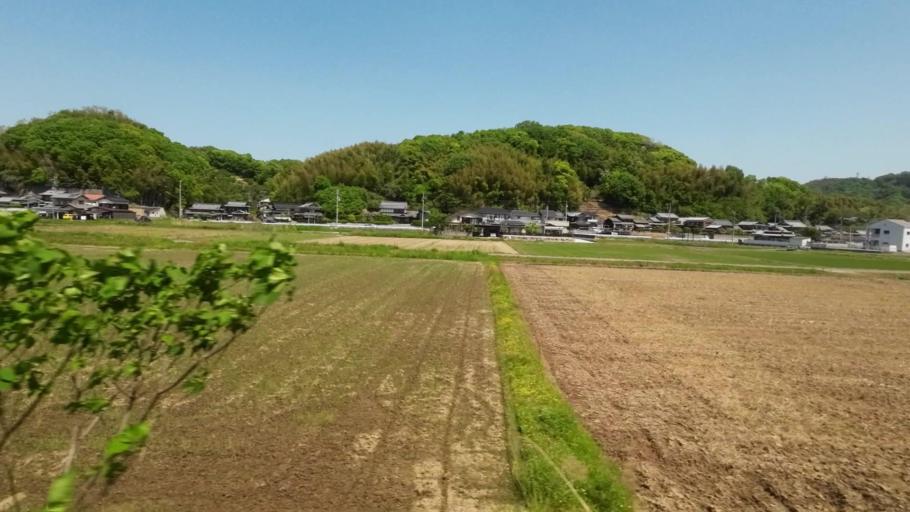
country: JP
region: Ehime
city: Hojo
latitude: 34.0953
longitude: 132.9444
